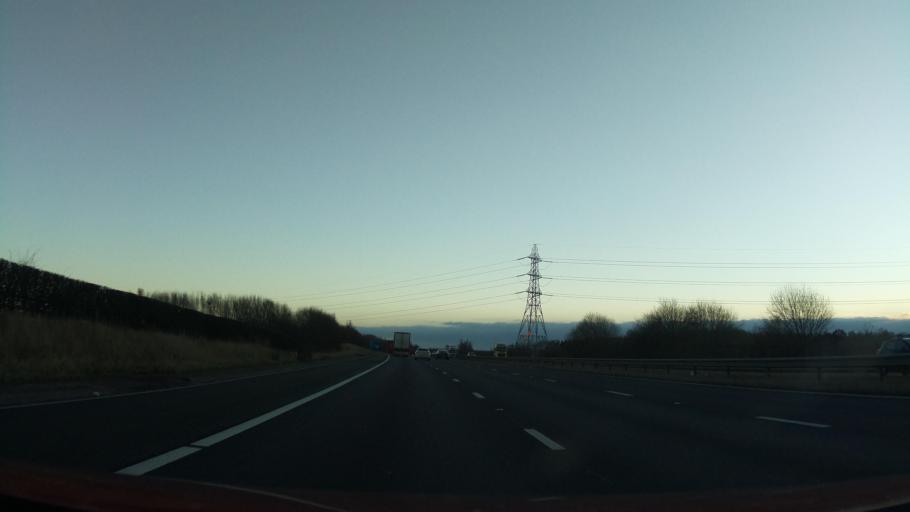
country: GB
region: England
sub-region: City and Borough of Leeds
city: Wetherby
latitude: 53.9586
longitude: -1.3701
